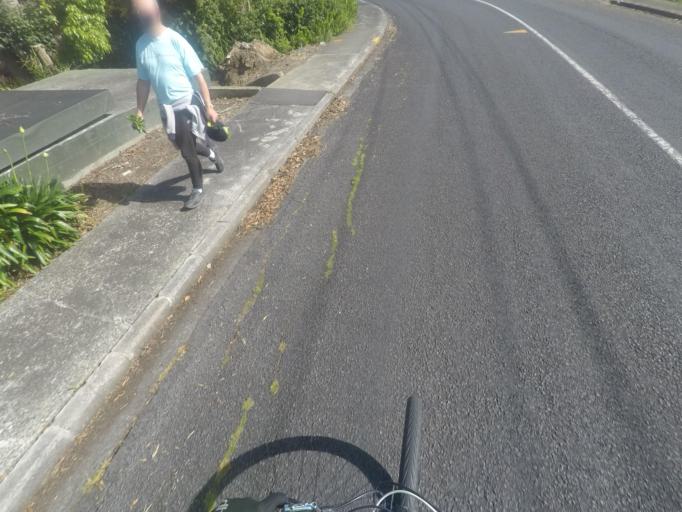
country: NZ
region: Auckland
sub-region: Auckland
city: Mangere
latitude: -36.9246
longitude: 174.7678
